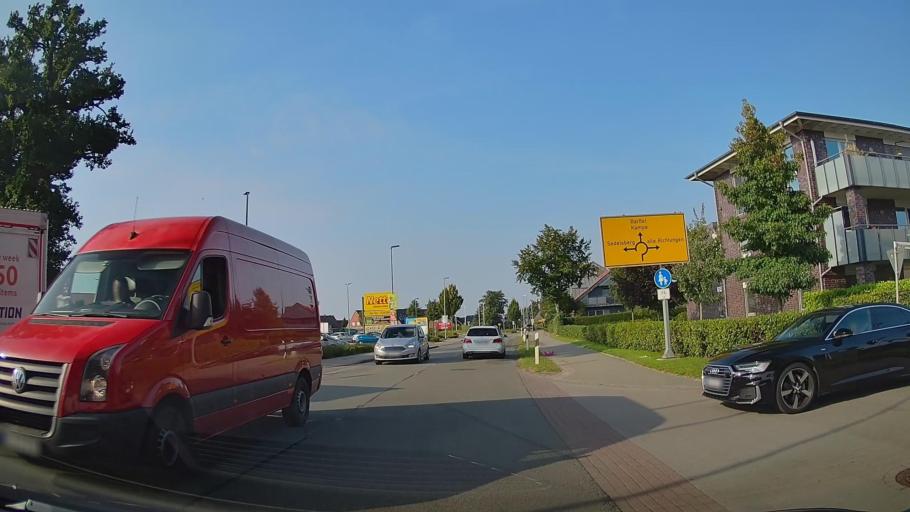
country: DE
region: Lower Saxony
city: Friesoythe
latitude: 53.0312
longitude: 7.8558
